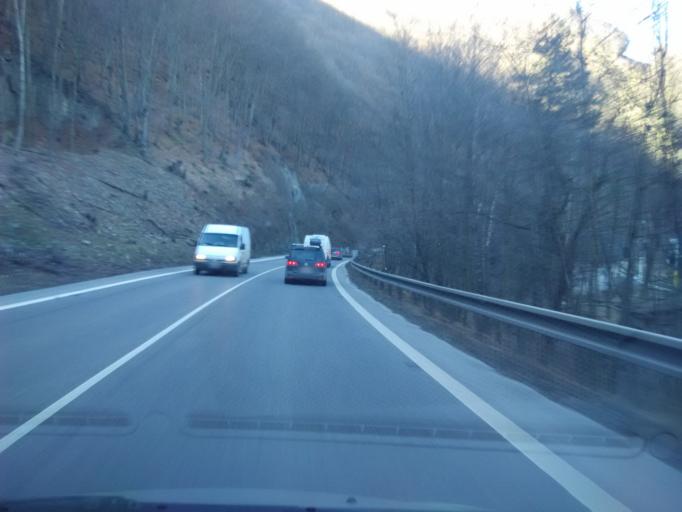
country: SK
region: Zilinsky
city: Krasnany
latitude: 49.1626
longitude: 18.8802
